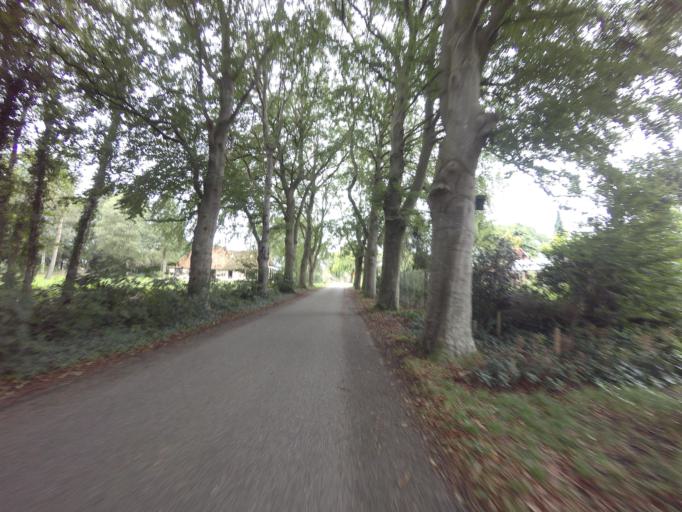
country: NL
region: Friesland
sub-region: Gemeente Weststellingwerf
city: Steggerda
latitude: 52.8863
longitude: 6.0877
